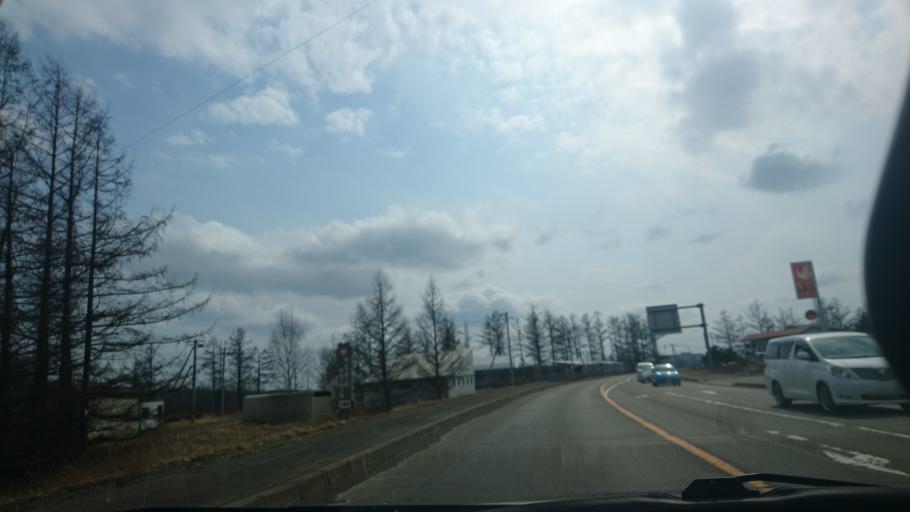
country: JP
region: Hokkaido
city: Otofuke
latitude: 43.1672
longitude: 143.2661
